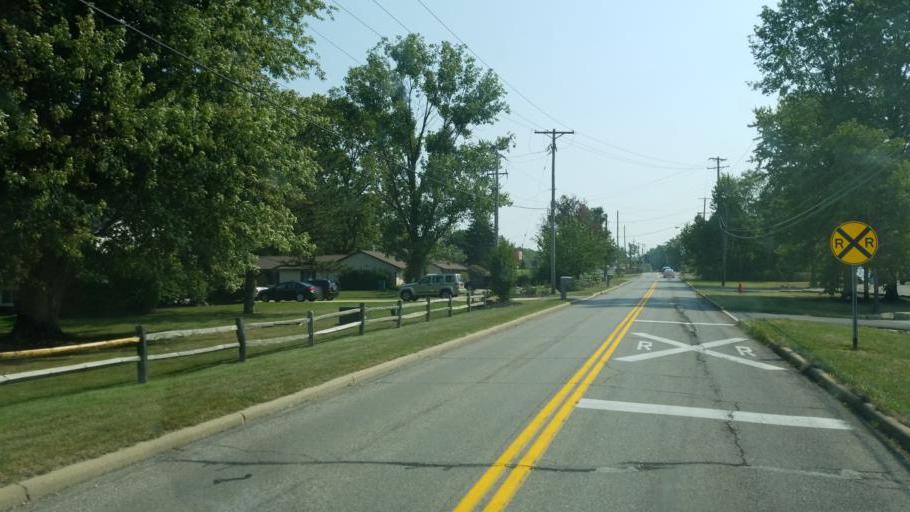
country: US
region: Ohio
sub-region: Lake County
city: Painesville
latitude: 41.7265
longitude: -81.2007
